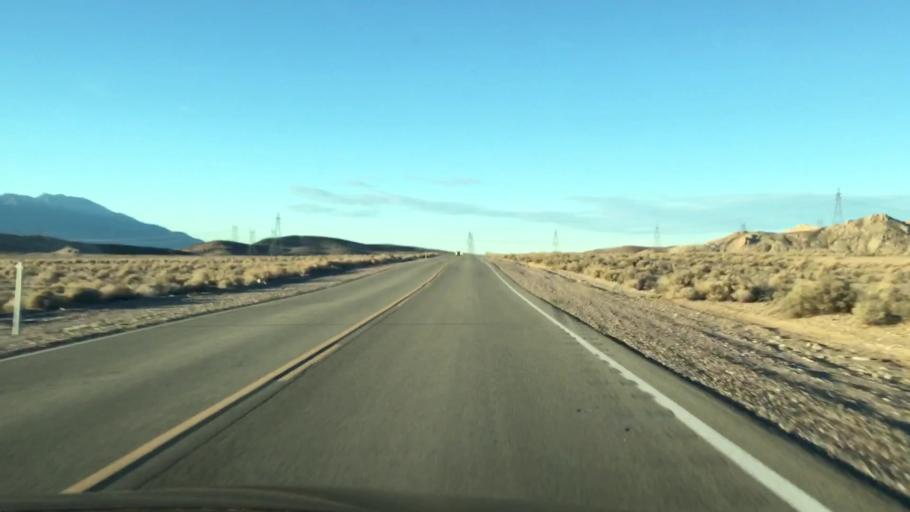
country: US
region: California
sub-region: San Bernardino County
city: Fort Irwin
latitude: 35.3780
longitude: -116.1222
